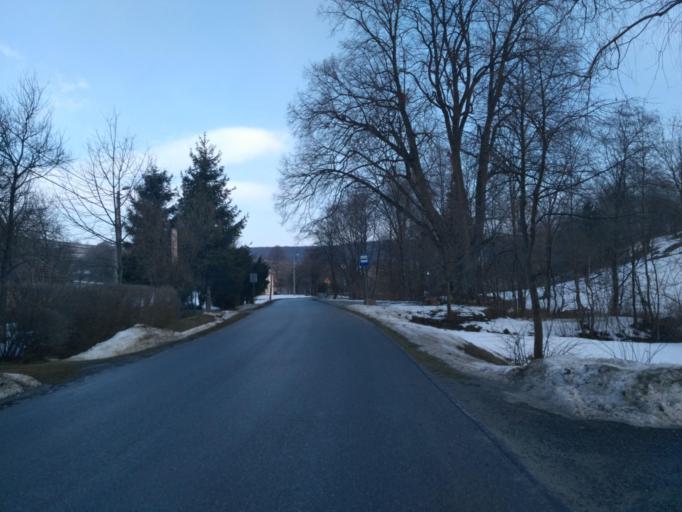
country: PL
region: Subcarpathian Voivodeship
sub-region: Powiat brzozowski
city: Dydnia
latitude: 49.6349
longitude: 22.1753
